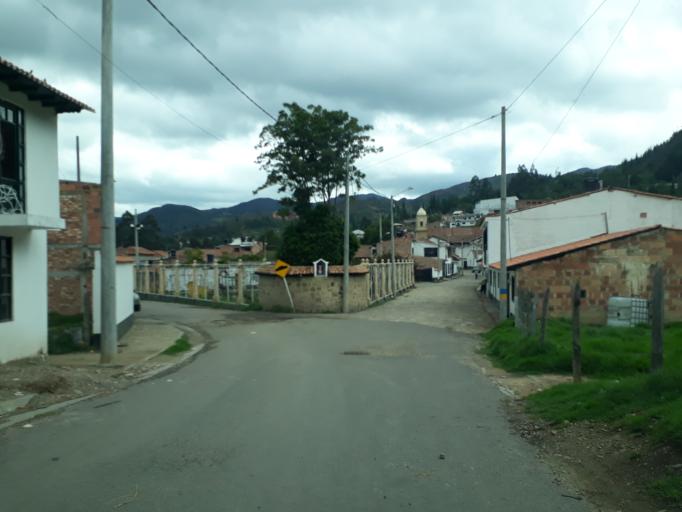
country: CO
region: Cundinamarca
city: Cucunuba
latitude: 5.2473
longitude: -73.7675
